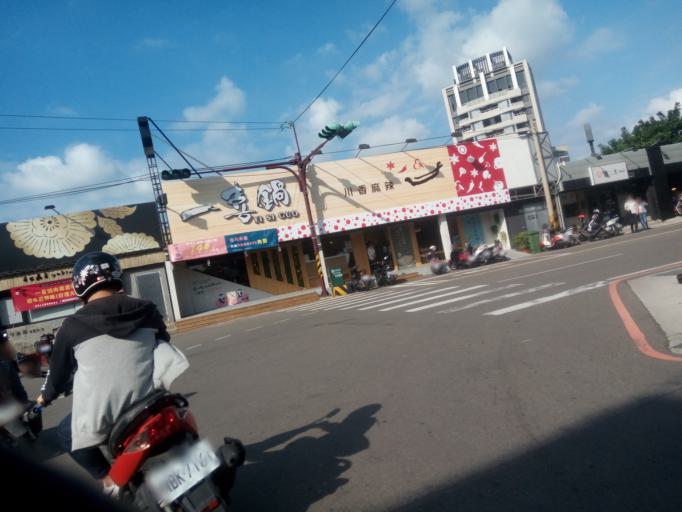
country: TW
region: Taiwan
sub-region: Hsinchu
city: Hsinchu
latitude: 24.6894
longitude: 120.9033
